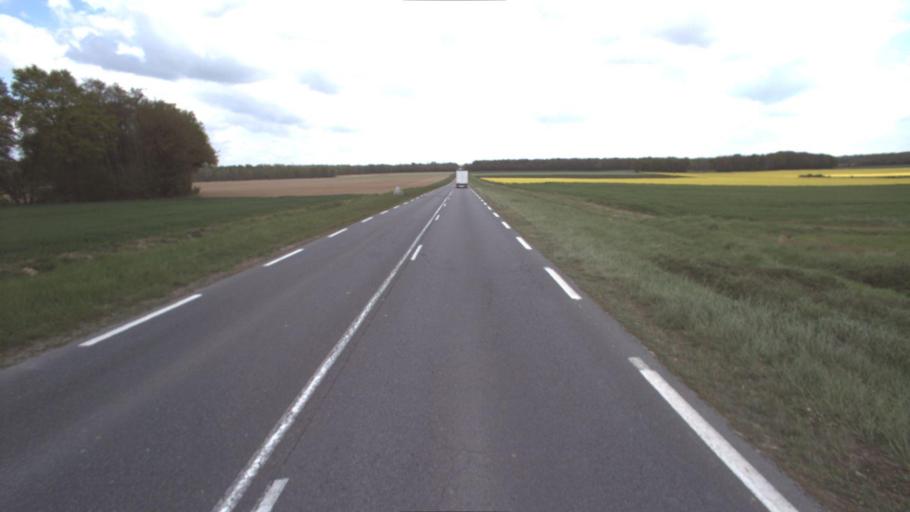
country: FR
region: Ile-de-France
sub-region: Departement de Seine-et-Marne
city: Villiers-Saint-Georges
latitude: 48.6982
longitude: 3.4476
